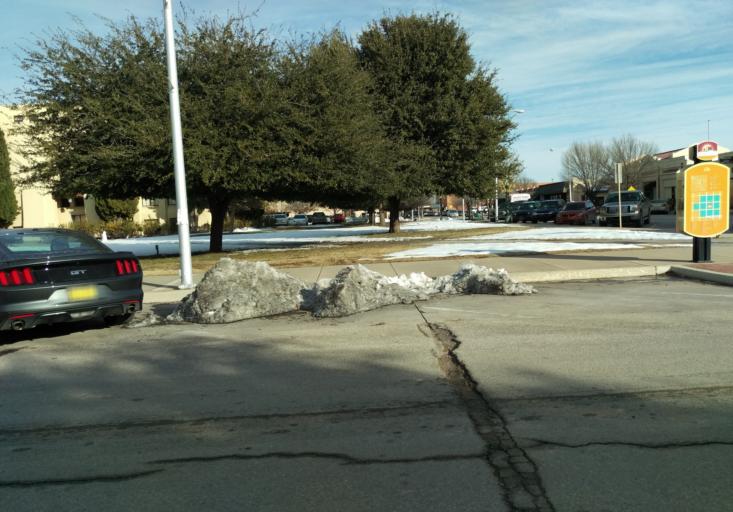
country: US
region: New Mexico
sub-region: Eddy County
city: Carlsbad
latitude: 32.4203
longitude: -104.2280
